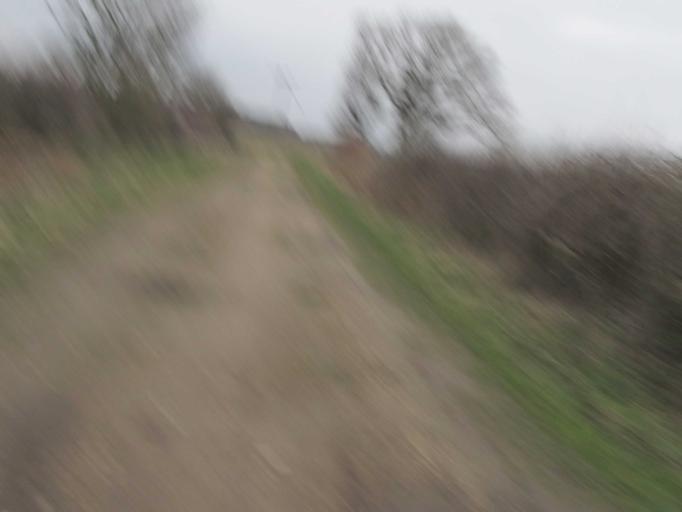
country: GB
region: England
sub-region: Doncaster
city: Bawtry
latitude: 53.4275
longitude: -0.9647
